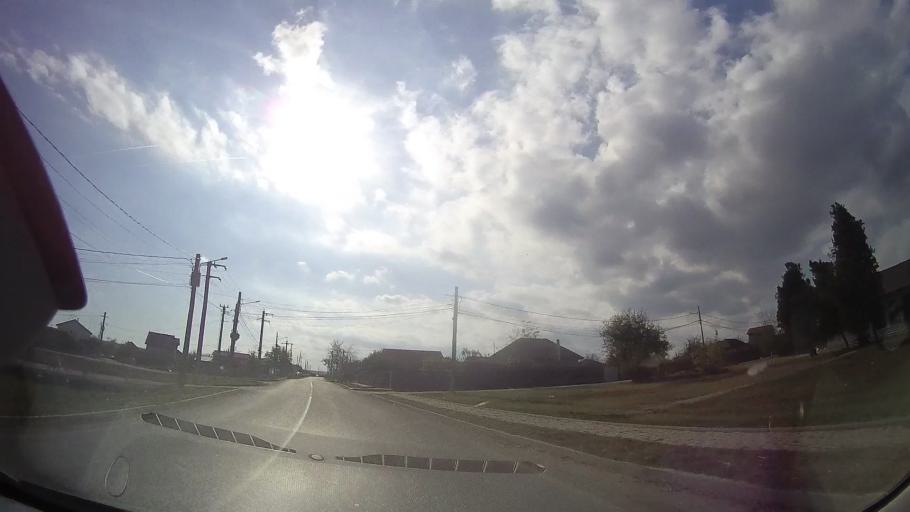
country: RO
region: Constanta
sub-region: Comuna Douazeci si Trei August
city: Dulcesti
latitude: 43.9112
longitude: 28.5504
